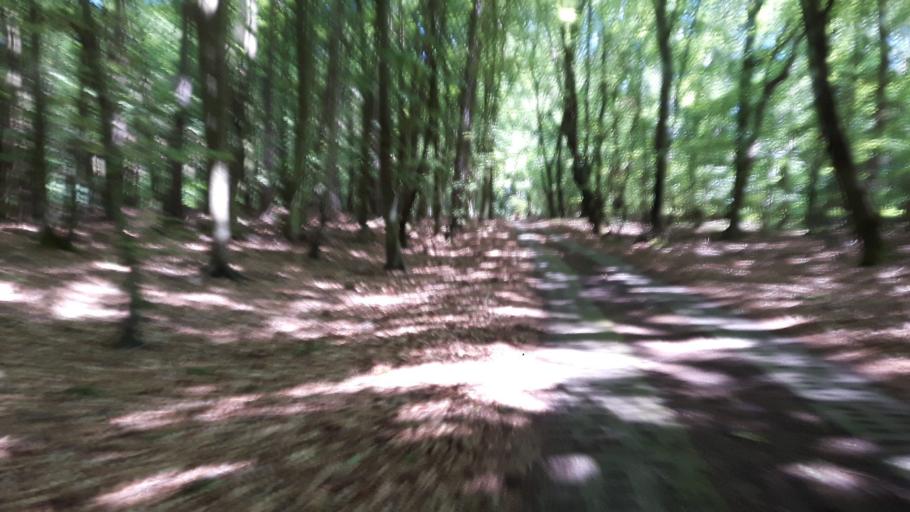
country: PL
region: Pomeranian Voivodeship
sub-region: Powiat slupski
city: Smoldzino
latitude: 54.6714
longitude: 17.1809
